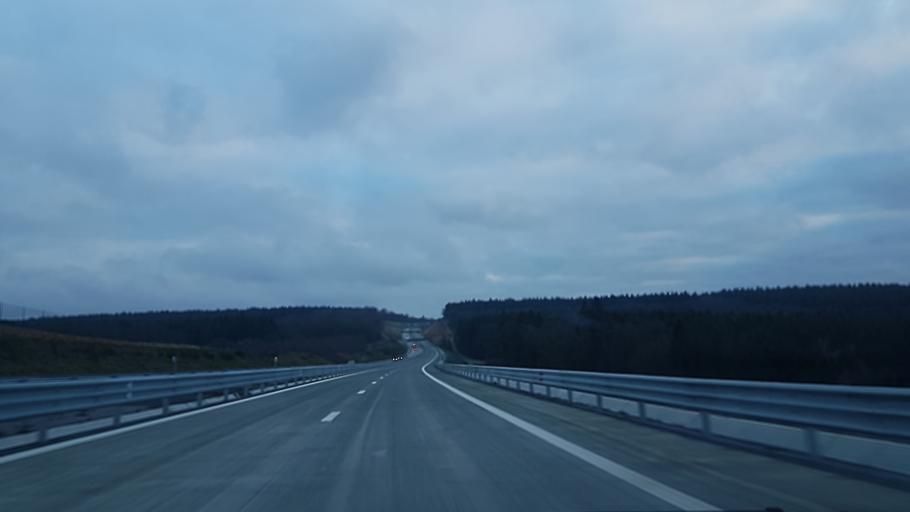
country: BE
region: Wallonia
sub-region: Province de Namur
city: Couvin
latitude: 50.0111
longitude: 4.5358
